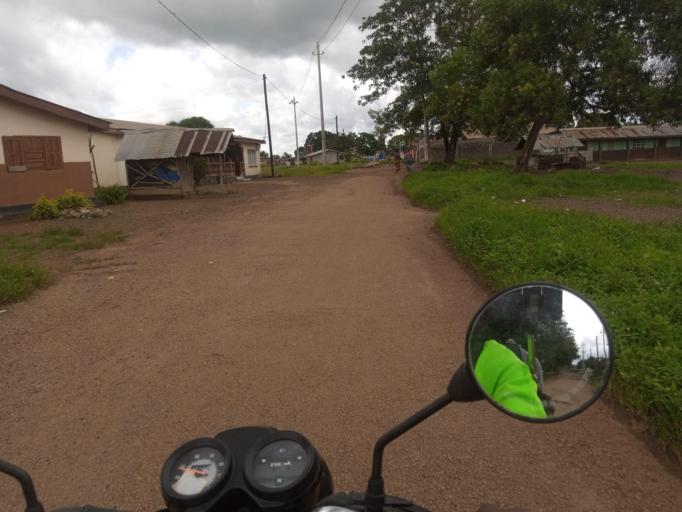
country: SL
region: Northern Province
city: Port Loko
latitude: 8.7655
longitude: -12.7794
